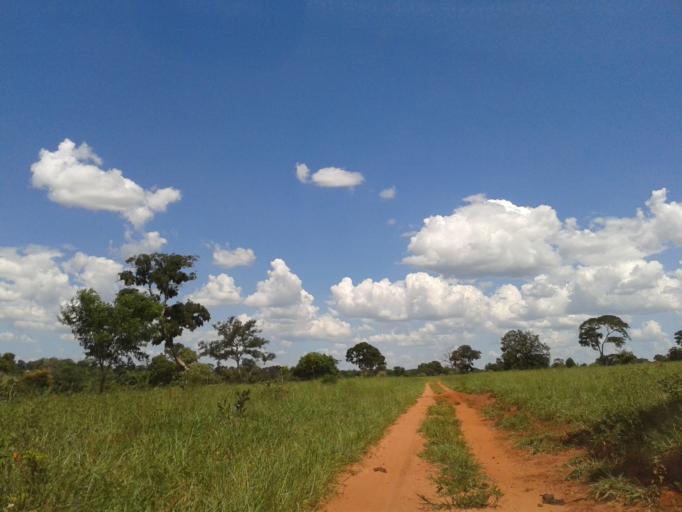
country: BR
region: Minas Gerais
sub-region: Santa Vitoria
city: Santa Vitoria
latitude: -19.1435
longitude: -50.5444
